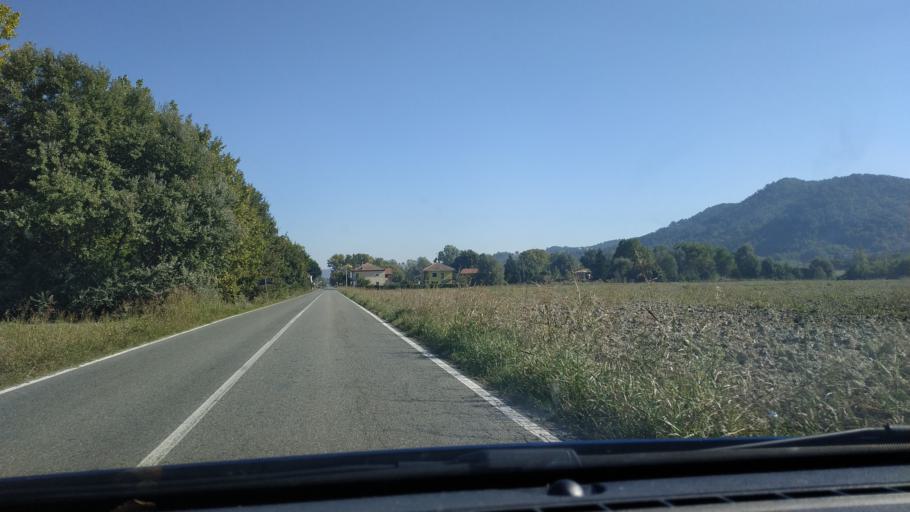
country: IT
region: Piedmont
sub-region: Provincia di Alessandria
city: Odalengo Grande
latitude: 45.0923
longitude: 8.1826
